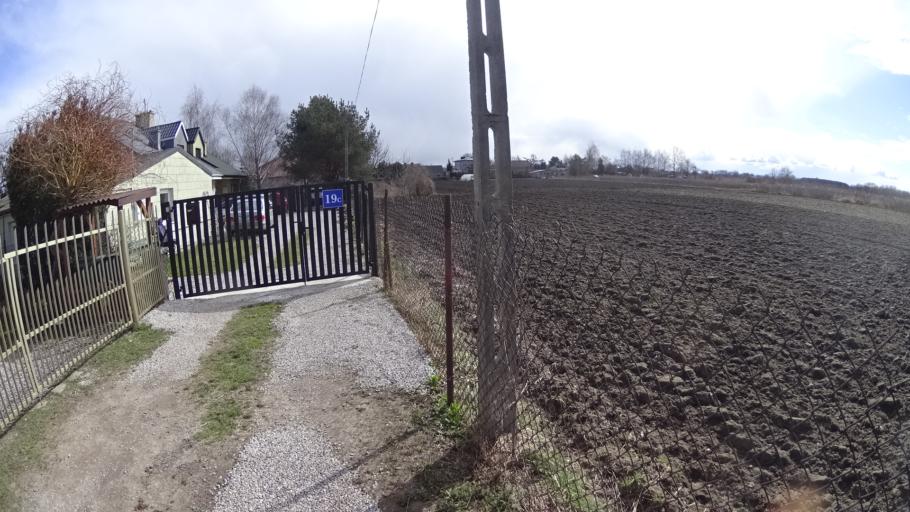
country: PL
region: Masovian Voivodeship
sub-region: Powiat warszawski zachodni
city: Jozefow
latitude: 52.2044
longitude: 20.6899
